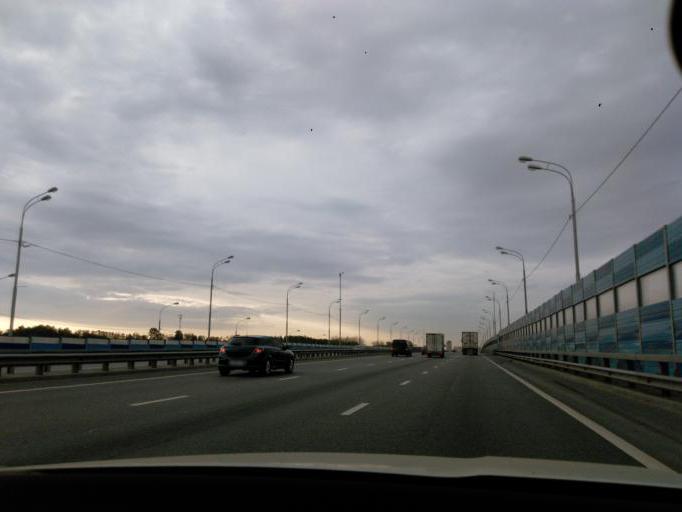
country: RU
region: Moscow
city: Severnyy
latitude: 55.9517
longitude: 37.5381
